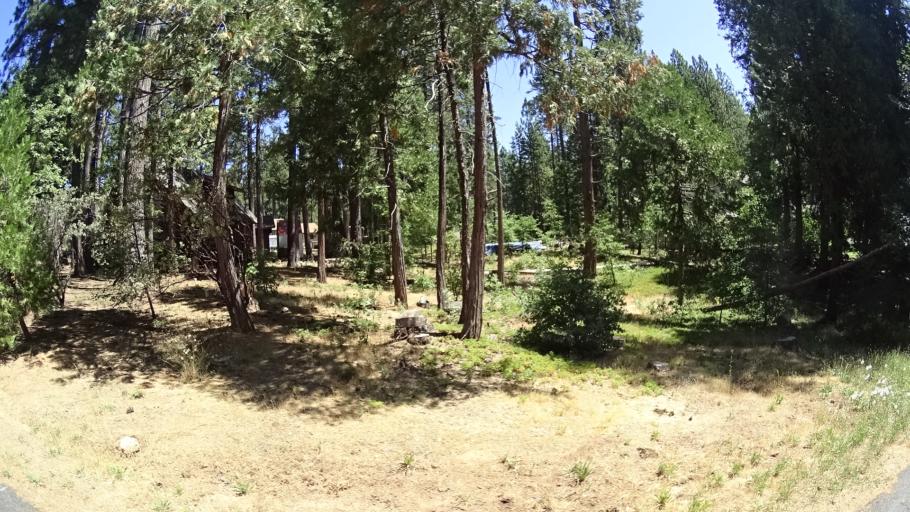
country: US
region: California
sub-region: Calaveras County
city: Forest Meadows
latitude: 38.2060
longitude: -120.3723
